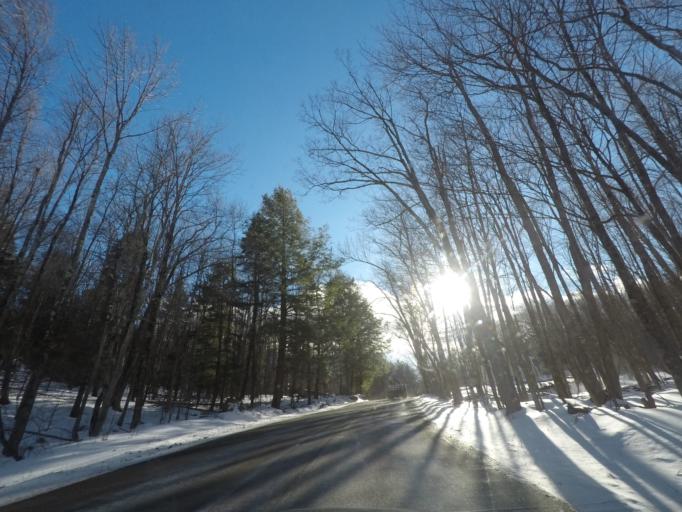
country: US
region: New York
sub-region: Rensselaer County
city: Hoosick Falls
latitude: 42.7872
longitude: -73.3985
